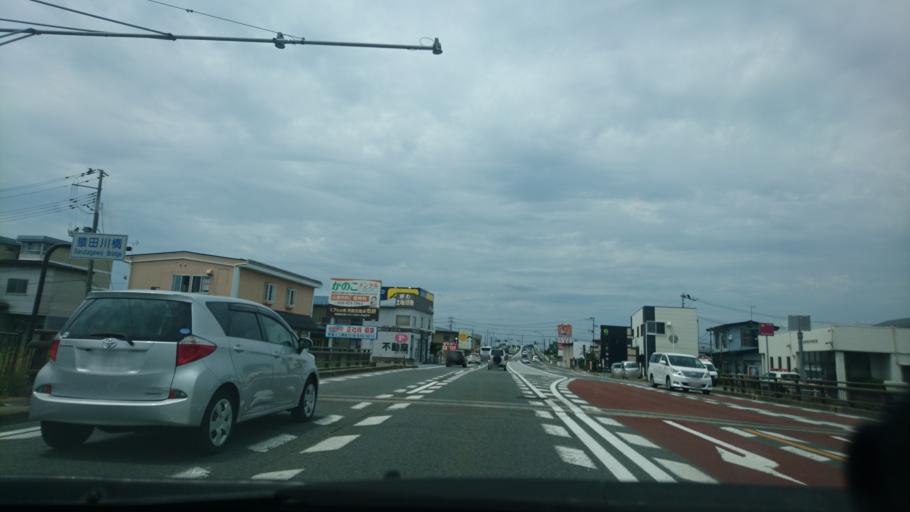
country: JP
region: Akita
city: Akita
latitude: 39.6923
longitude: 140.1217
